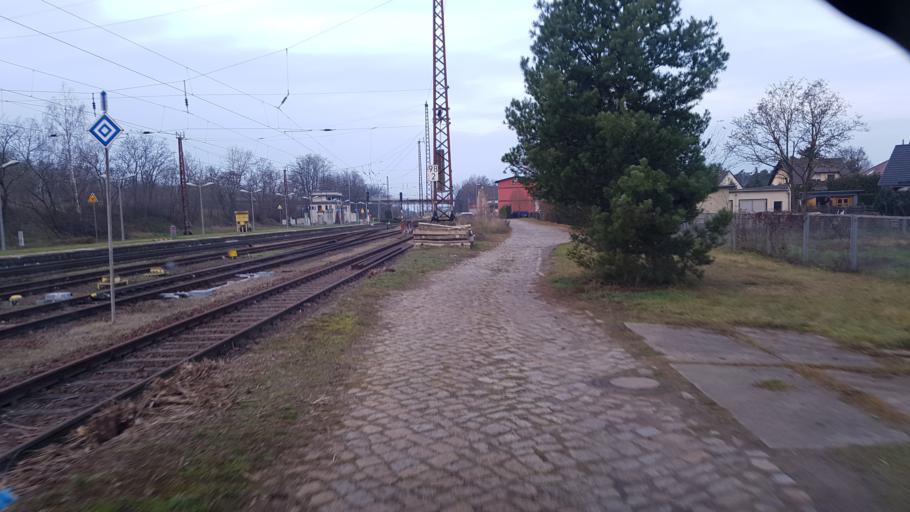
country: DE
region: Brandenburg
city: Ziltendorf
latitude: 52.1986
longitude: 14.6175
